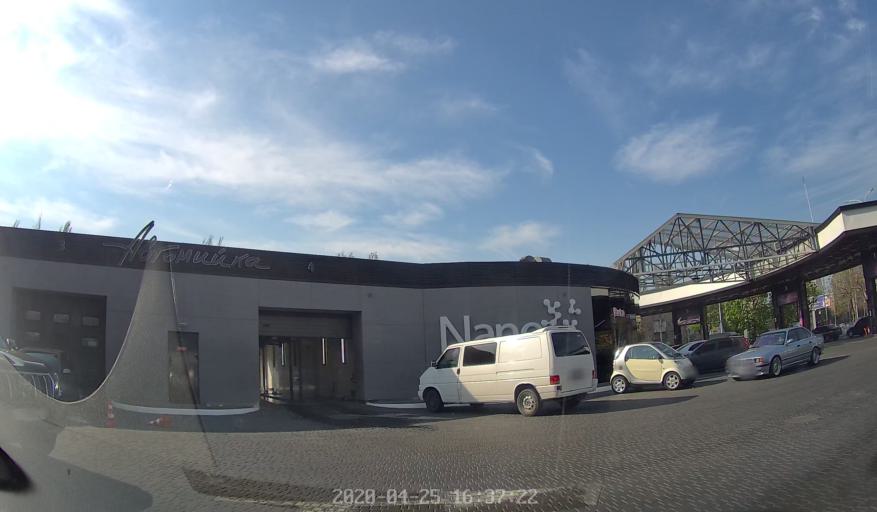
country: GR
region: South Aegean
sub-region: Nomos Kykladon
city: Serifos
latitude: 37.1397
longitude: 24.5790
